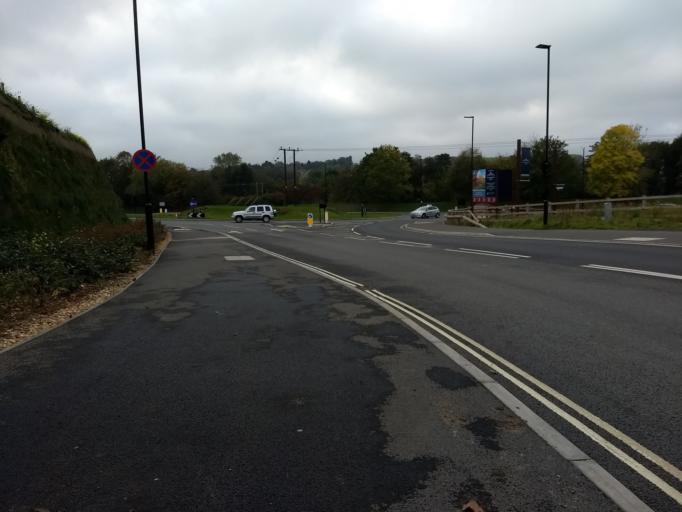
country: GB
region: England
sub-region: Isle of Wight
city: Newport
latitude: 50.6934
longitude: -1.2865
